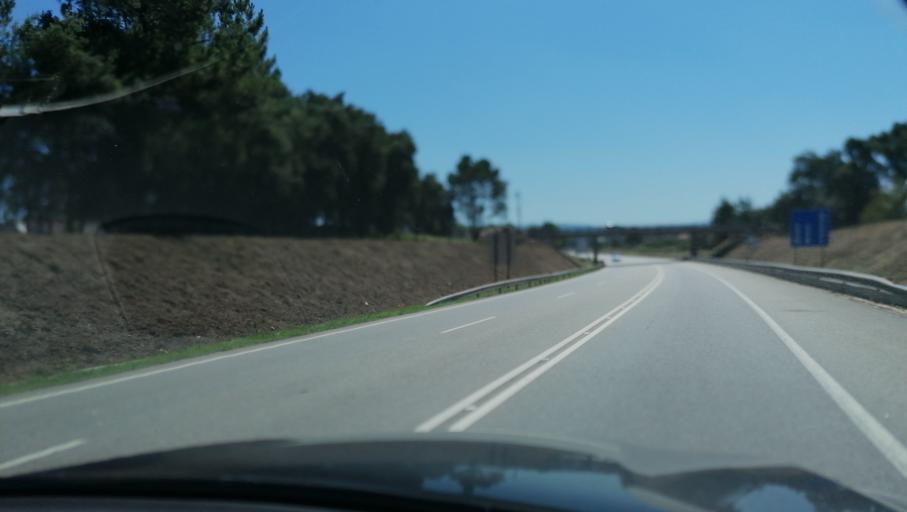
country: PT
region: Aveiro
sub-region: Oliveira do Bairro
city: Oliveira do Bairro
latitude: 40.5430
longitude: -8.4677
